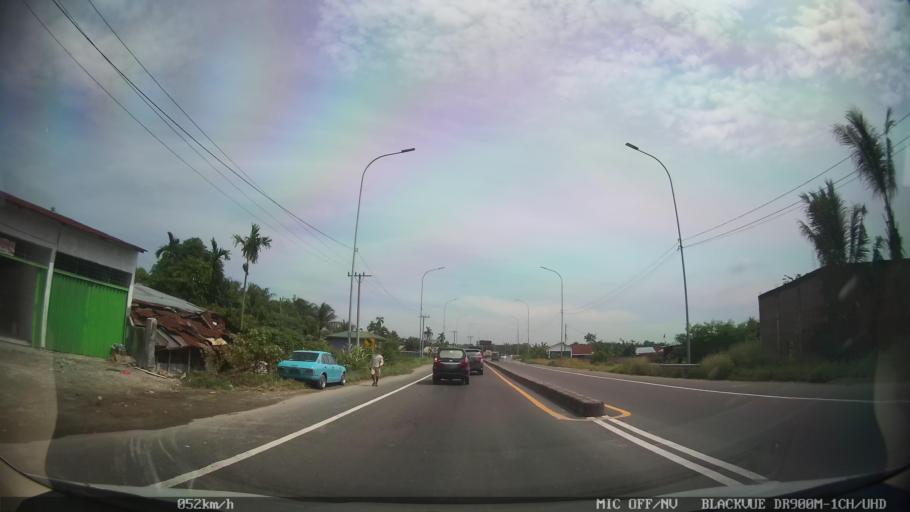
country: ID
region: North Sumatra
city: Sunggal
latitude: 3.6190
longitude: 98.6287
